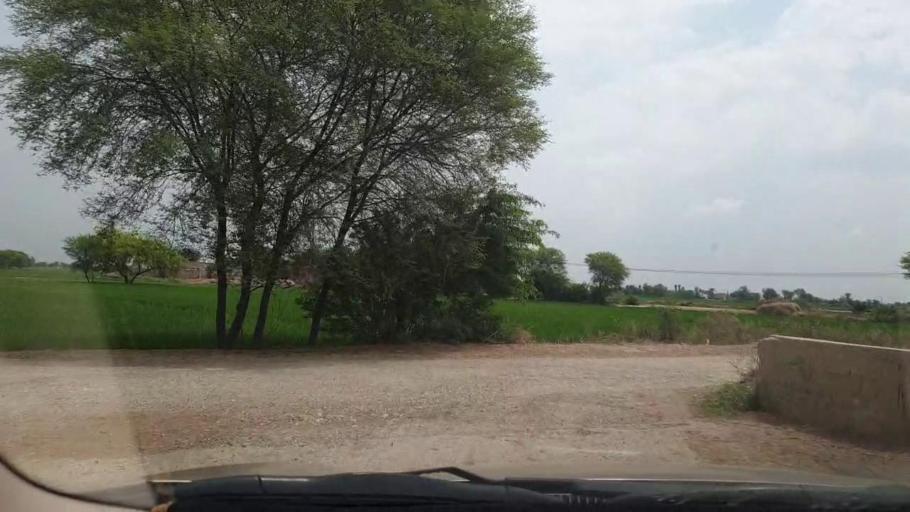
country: PK
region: Sindh
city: Larkana
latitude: 27.5478
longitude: 68.1643
